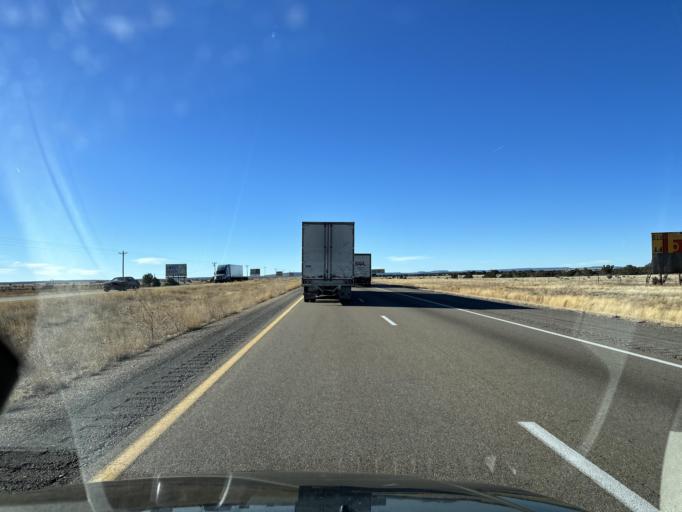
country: US
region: New Mexico
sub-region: San Miguel County
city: Las Vegas
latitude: 34.9938
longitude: -105.3357
